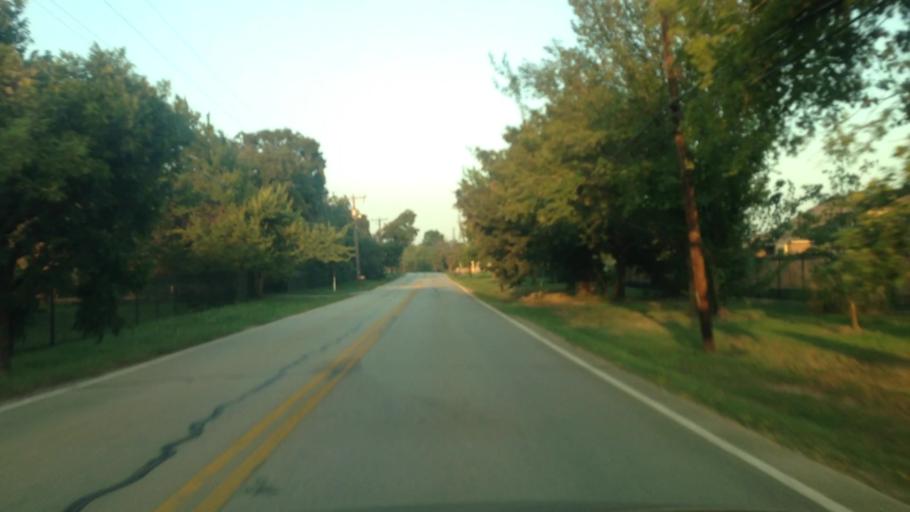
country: US
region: Texas
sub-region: Tarrant County
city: Kennedale
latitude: 32.6332
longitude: -97.1920
